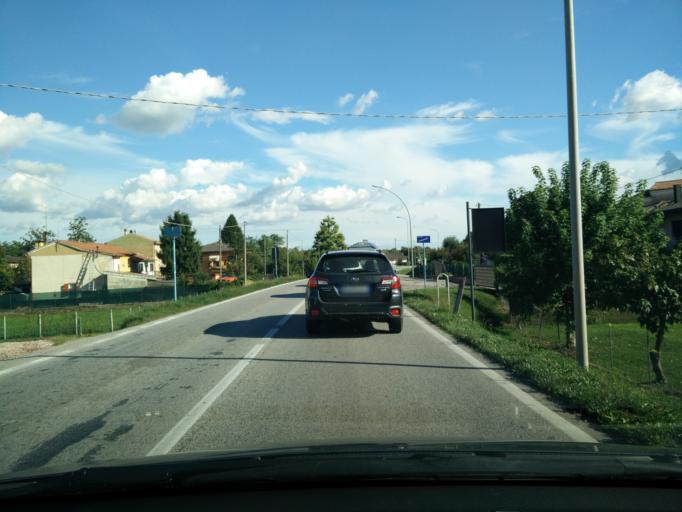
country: IT
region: Veneto
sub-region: Provincia di Treviso
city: Saletto-San Bartolomeo
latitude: 45.7272
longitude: 12.3998
